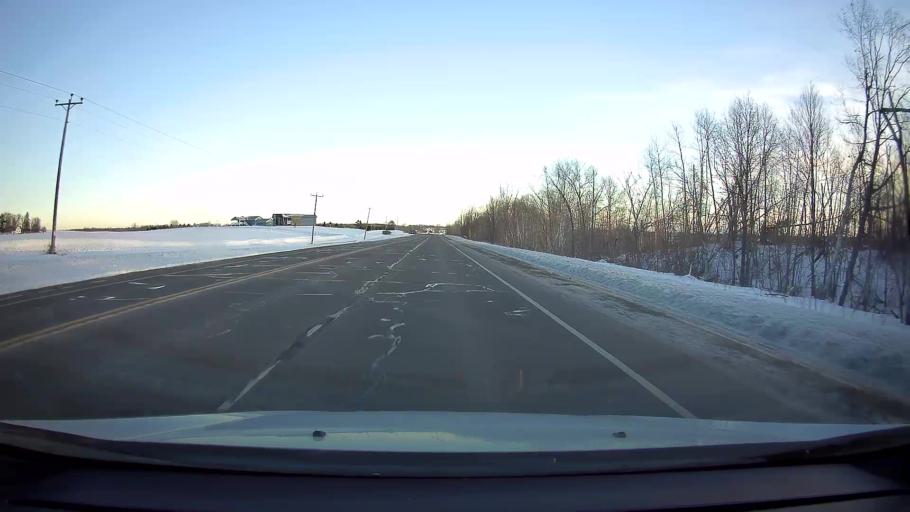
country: US
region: Wisconsin
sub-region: Barron County
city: Cumberland
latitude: 45.4891
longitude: -92.0599
